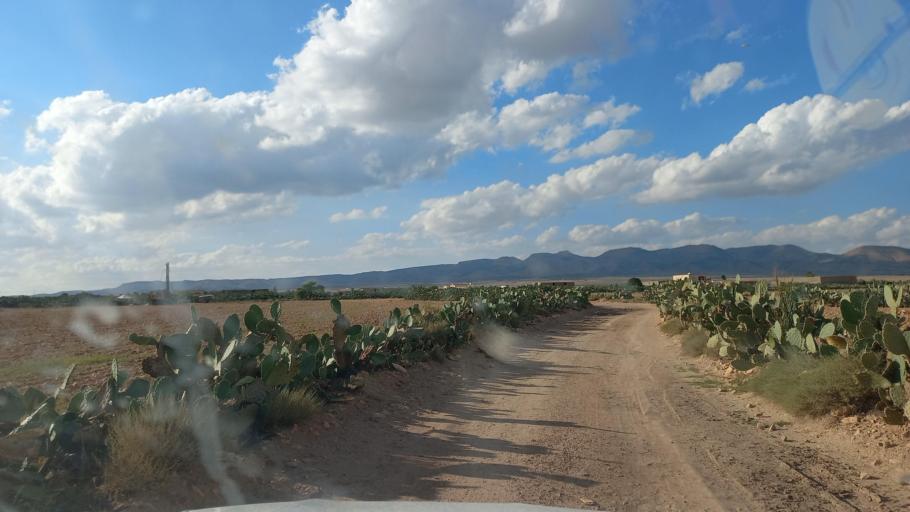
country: TN
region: Al Qasrayn
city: Sbiba
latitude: 35.3873
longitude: 9.0694
